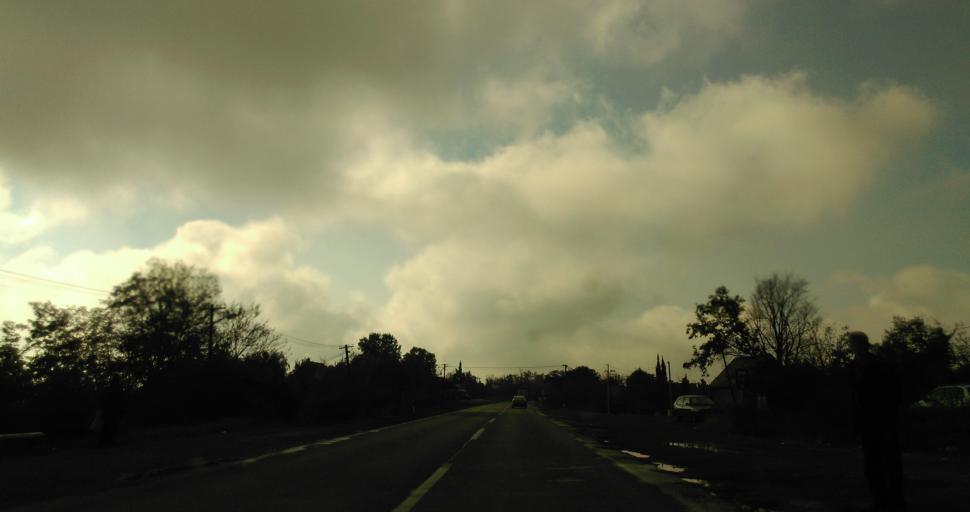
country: RS
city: Vranic
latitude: 44.5662
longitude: 20.3014
